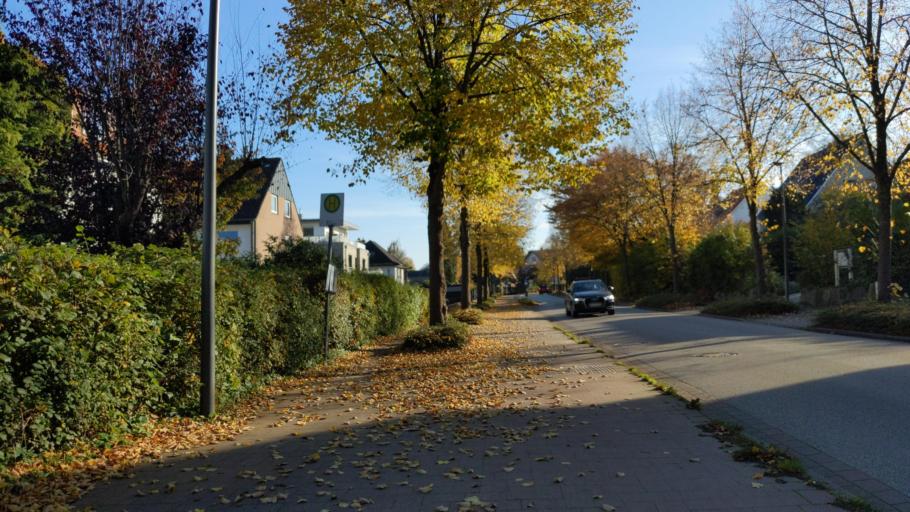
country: DE
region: Schleswig-Holstein
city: Eutin
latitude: 54.1476
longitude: 10.6092
